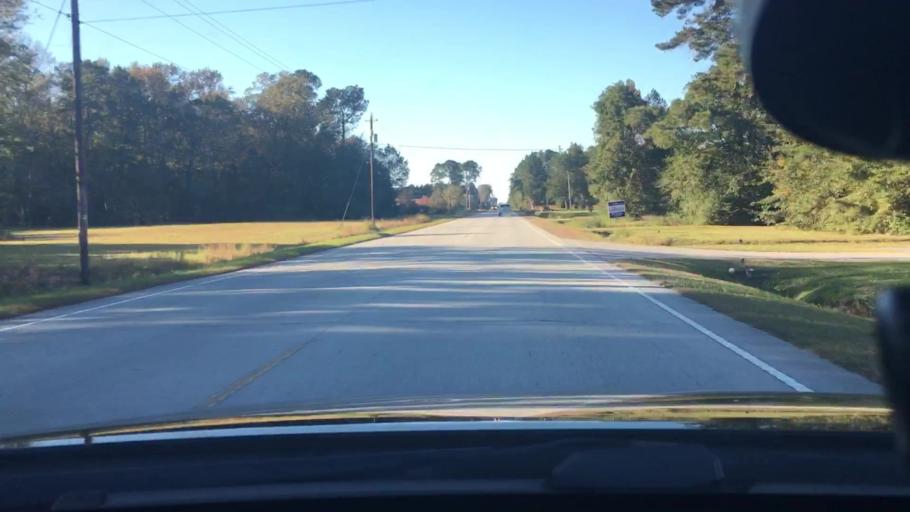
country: US
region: North Carolina
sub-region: Craven County
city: Vanceboro
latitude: 35.3556
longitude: -77.1924
